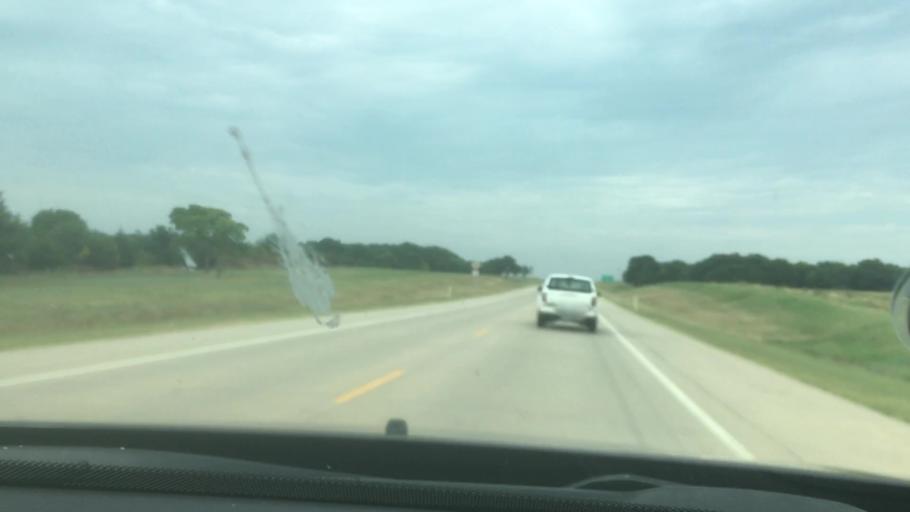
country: US
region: Oklahoma
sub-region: Murray County
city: Sulphur
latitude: 34.6131
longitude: -96.8746
